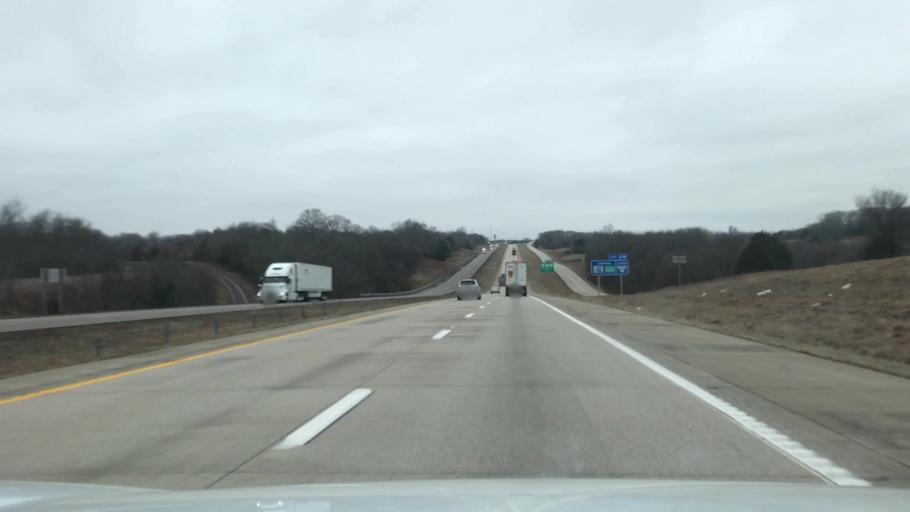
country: US
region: Missouri
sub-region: Crawford County
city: Bourbon
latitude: 38.1632
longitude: -91.2277
